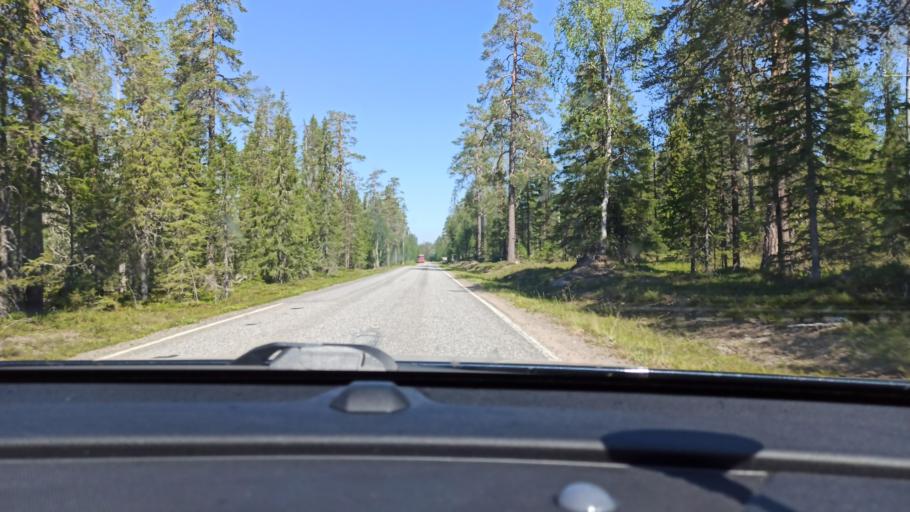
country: FI
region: Lapland
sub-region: Tunturi-Lappi
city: Kolari
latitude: 67.6631
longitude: 24.1633
